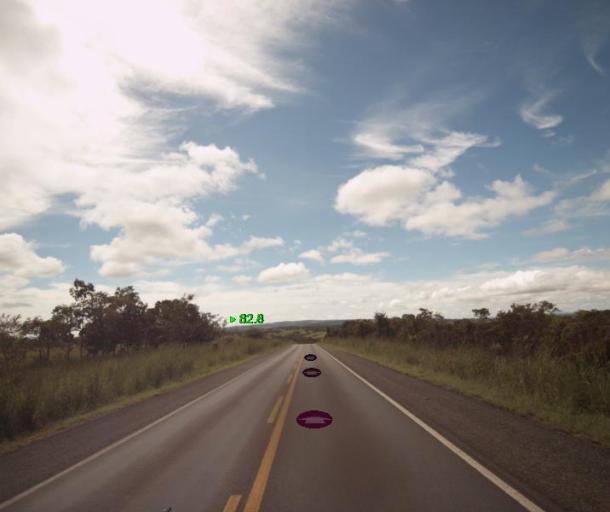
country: BR
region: Goias
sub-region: Padre Bernardo
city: Padre Bernardo
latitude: -15.2152
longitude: -48.5955
